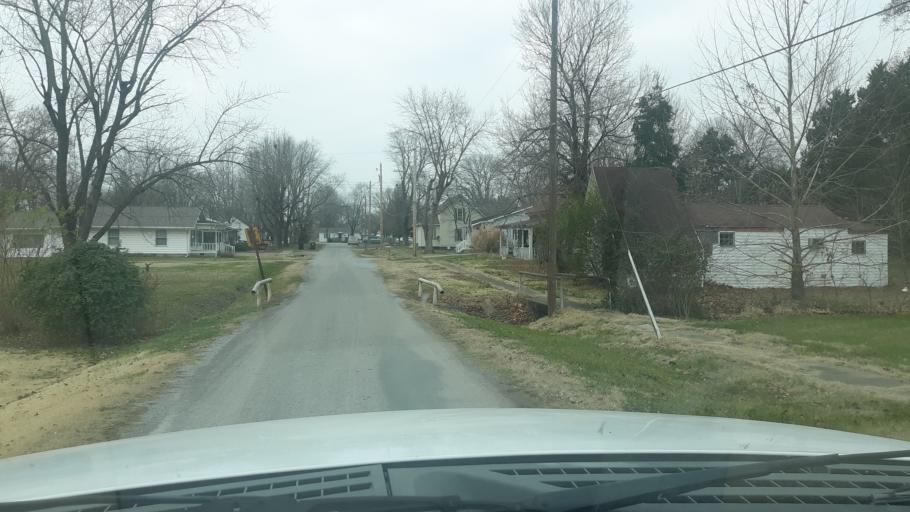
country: US
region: Illinois
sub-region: Saline County
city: Harrisburg
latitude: 37.8390
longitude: -88.6072
